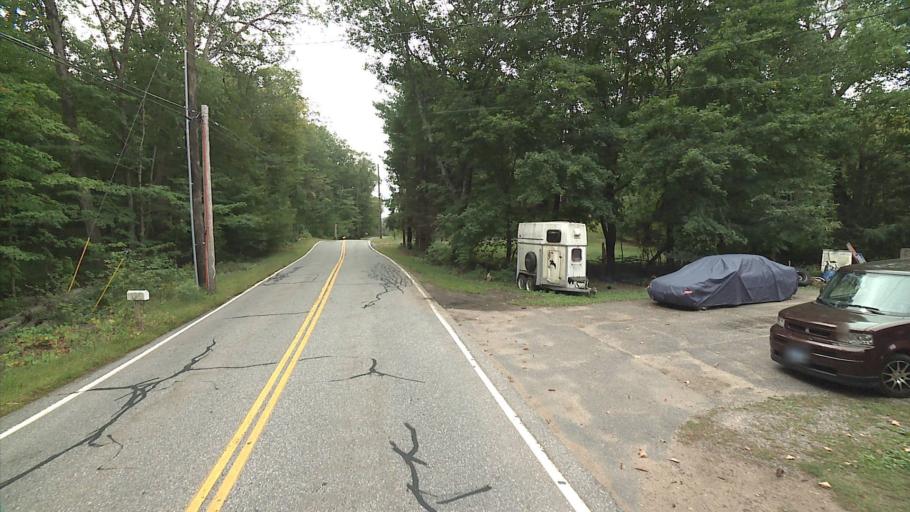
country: US
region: Connecticut
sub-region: Tolland County
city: Storrs
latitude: 41.8712
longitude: -72.2653
